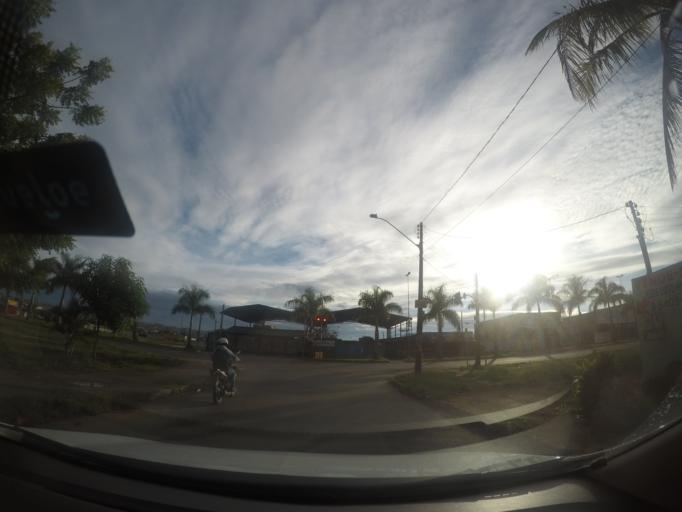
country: BR
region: Goias
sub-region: Goiania
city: Goiania
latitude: -16.6401
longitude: -49.3167
